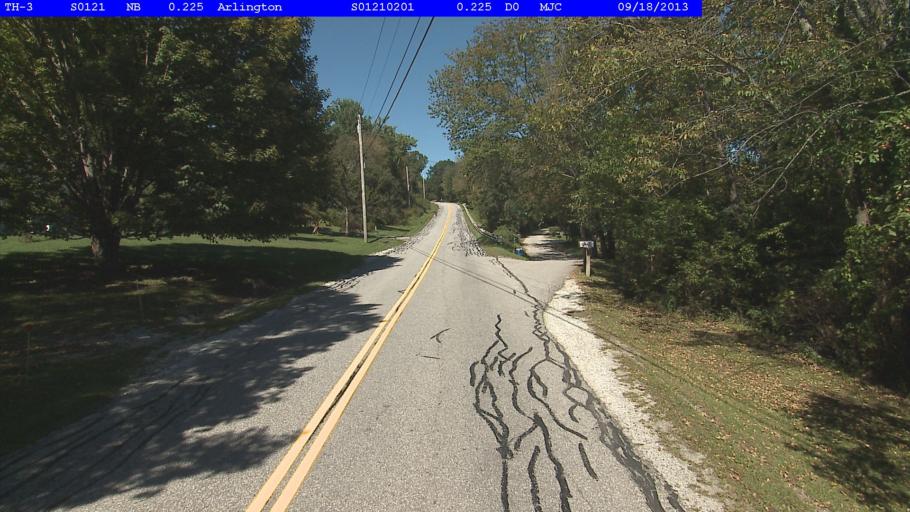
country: US
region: Vermont
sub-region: Bennington County
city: Arlington
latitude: 43.1067
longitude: -73.2125
